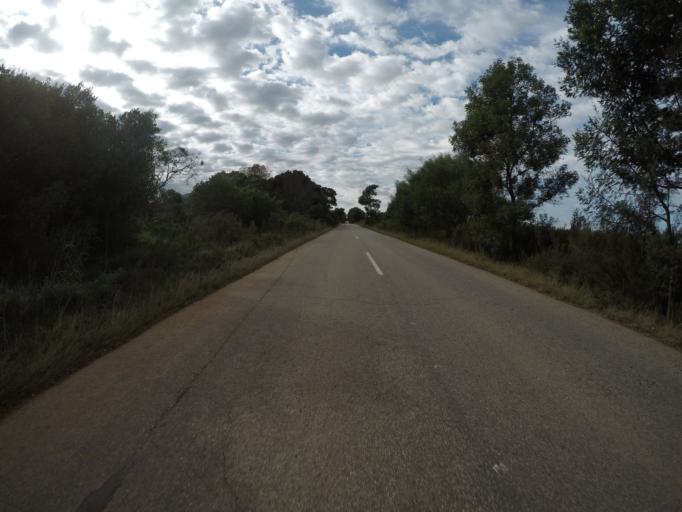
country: ZA
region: Eastern Cape
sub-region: Cacadu District Municipality
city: Kareedouw
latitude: -34.0446
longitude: 24.4377
